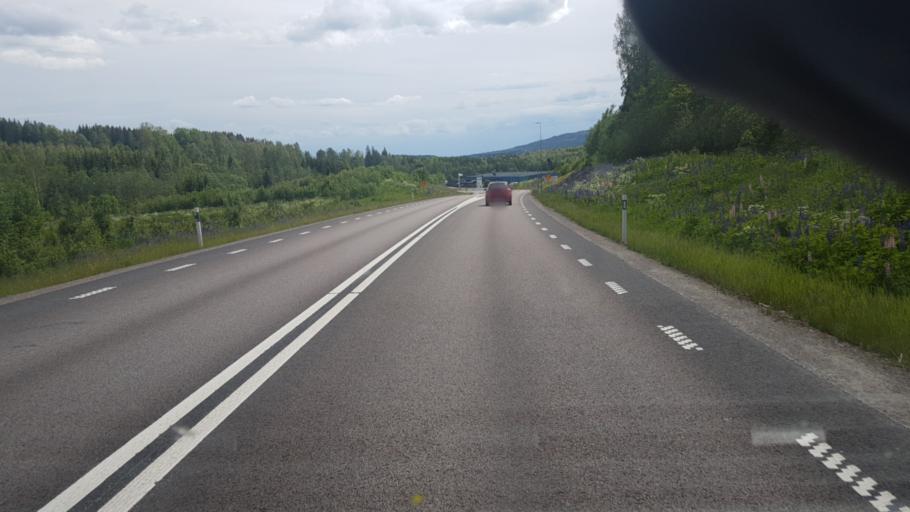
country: SE
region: Vaermland
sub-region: Eda Kommun
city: Amotfors
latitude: 59.7735
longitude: 12.3766
